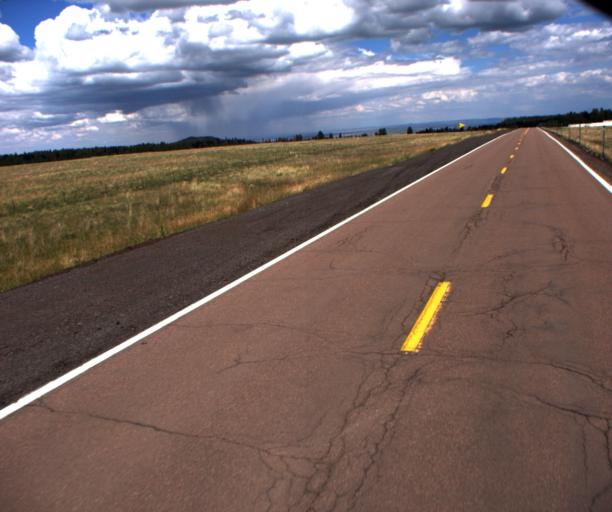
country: US
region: Arizona
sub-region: Apache County
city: Eagar
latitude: 34.0541
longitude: -109.5159
